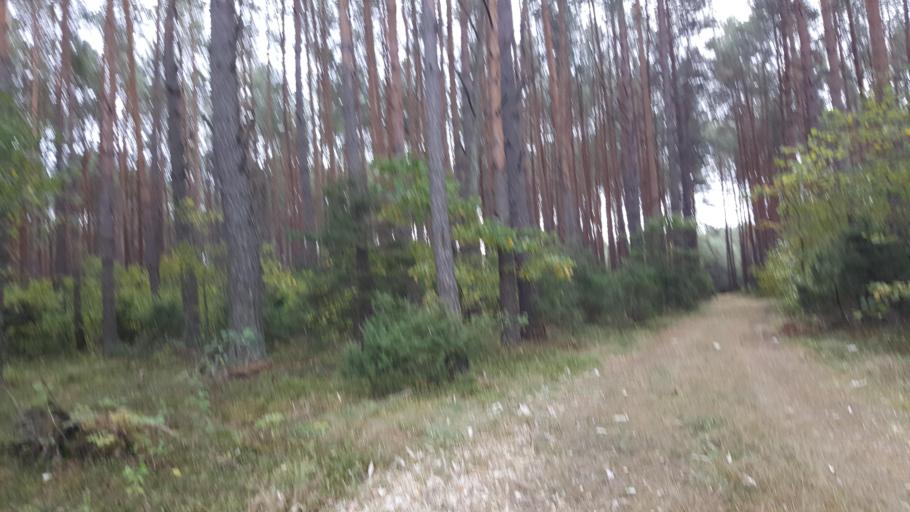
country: BY
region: Brest
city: Kamyanyets
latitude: 52.4276
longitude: 23.9038
